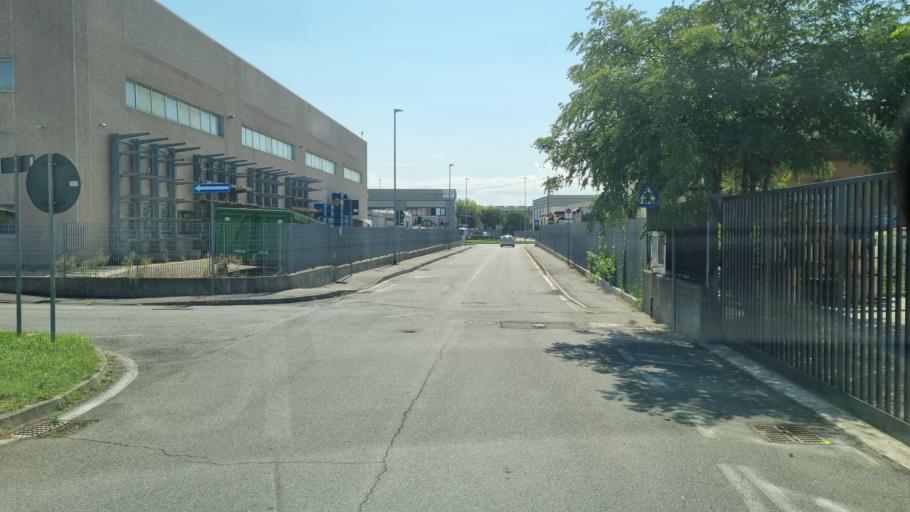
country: IT
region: Lombardy
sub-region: Provincia di Bergamo
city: Comun Nuovo
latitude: 45.6200
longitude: 9.6461
